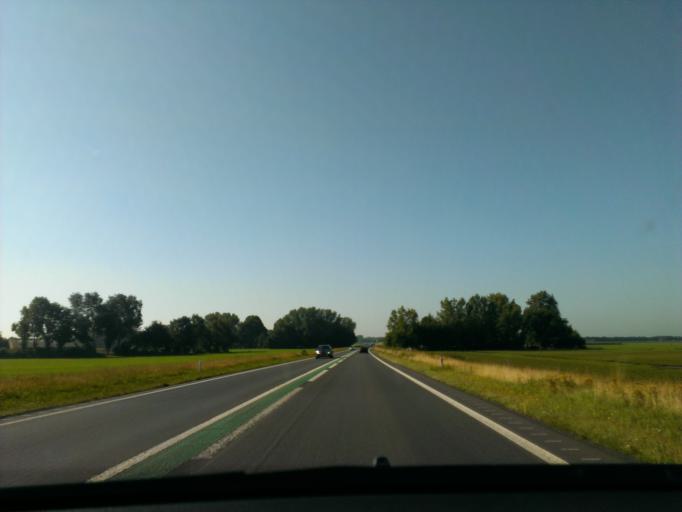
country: NL
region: Drenthe
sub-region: Gemeente Coevorden
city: Dalen
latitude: 52.6939
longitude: 6.7421
